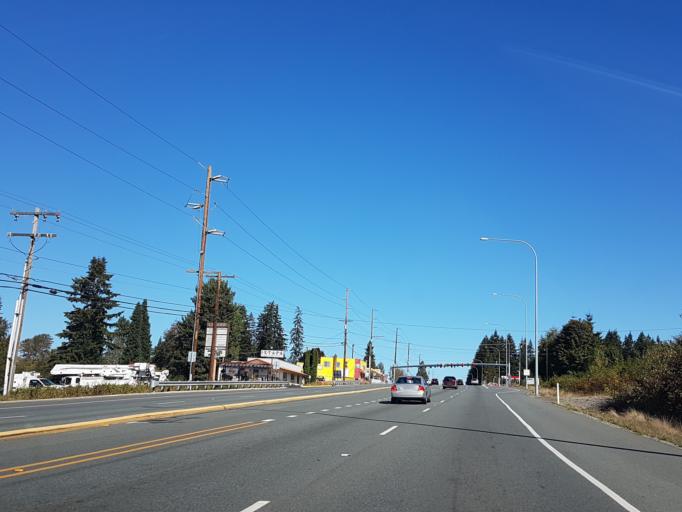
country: US
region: Washington
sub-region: Snohomish County
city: Clearview
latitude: 47.8316
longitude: -122.1273
